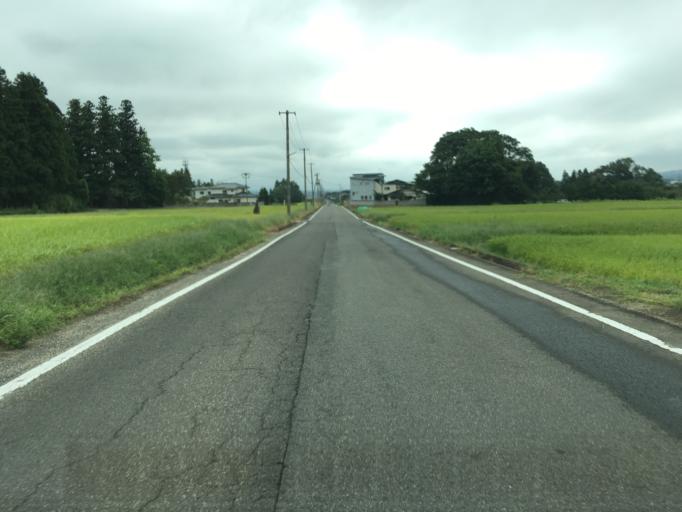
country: JP
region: Fukushima
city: Fukushima-shi
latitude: 37.7630
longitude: 140.3923
